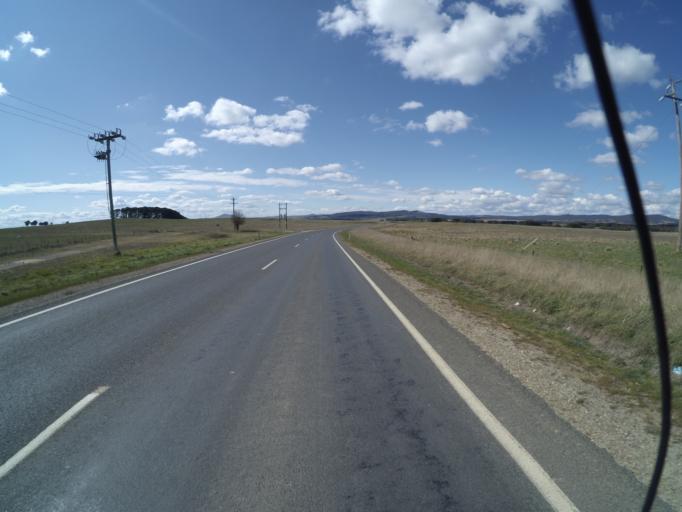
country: AU
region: New South Wales
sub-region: Palerang
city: Bungendore
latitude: -35.2176
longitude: 149.4650
